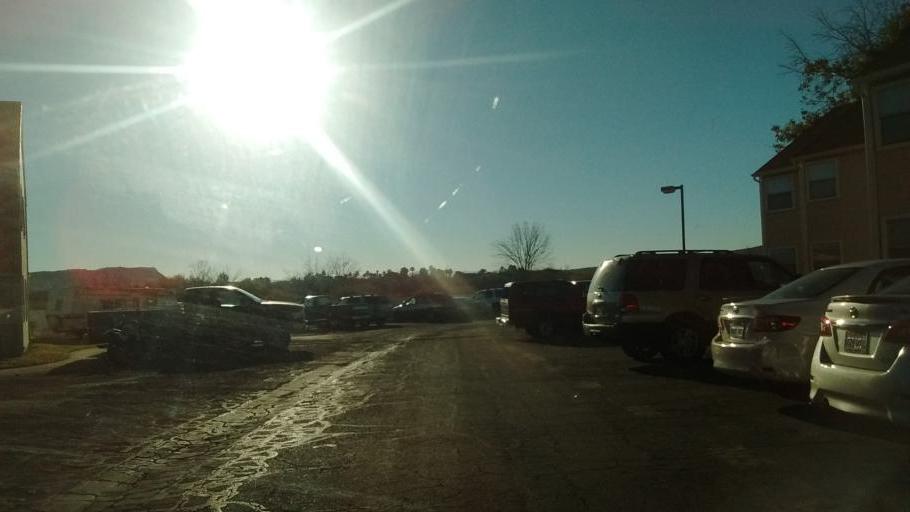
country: US
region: Utah
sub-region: Washington County
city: Saint George
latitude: 37.0844
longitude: -113.5733
